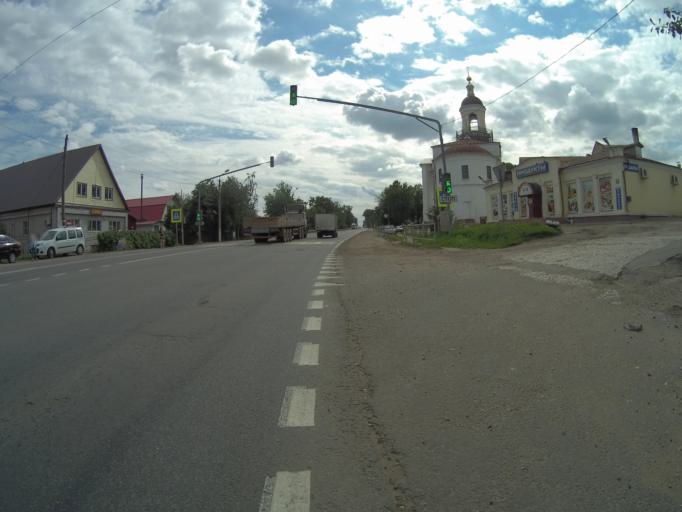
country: RU
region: Vladimir
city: Bogolyubovo
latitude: 56.1951
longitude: 40.5331
